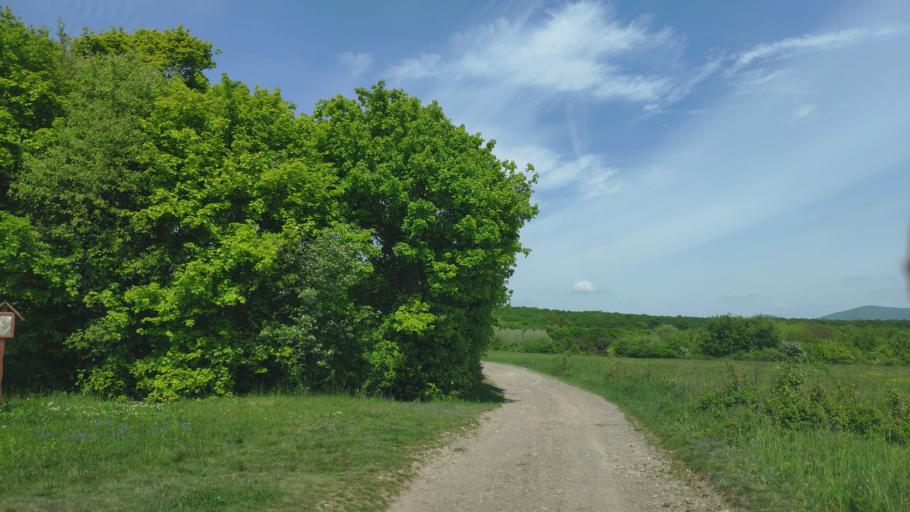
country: SK
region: Kosicky
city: Secovce
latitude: 48.6984
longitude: 21.5944
